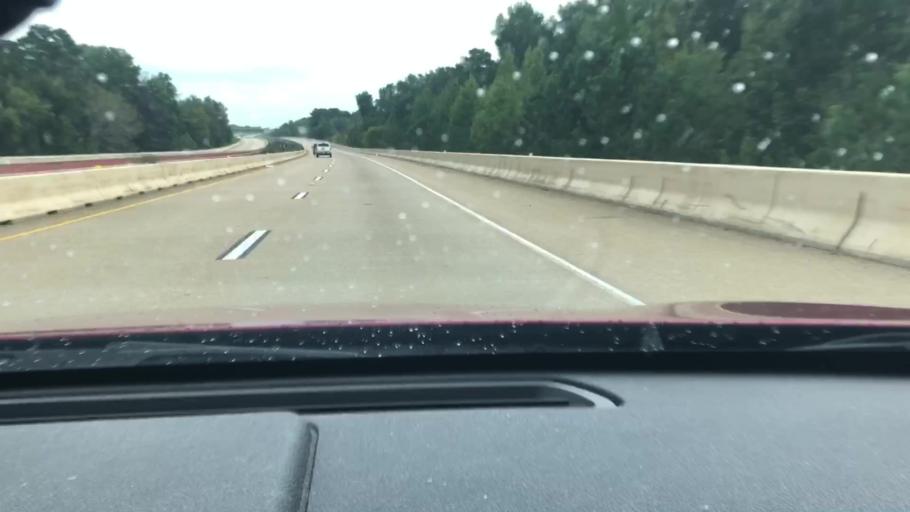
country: US
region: Texas
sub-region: Bowie County
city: Texarkana
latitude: 33.3851
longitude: -94.0580
